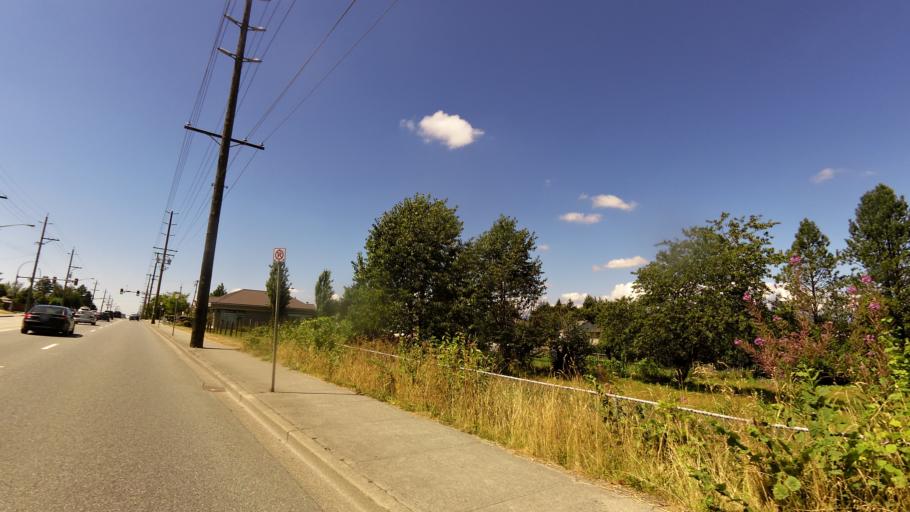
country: CA
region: British Columbia
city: Maple Ridge
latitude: 49.2205
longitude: -122.5831
